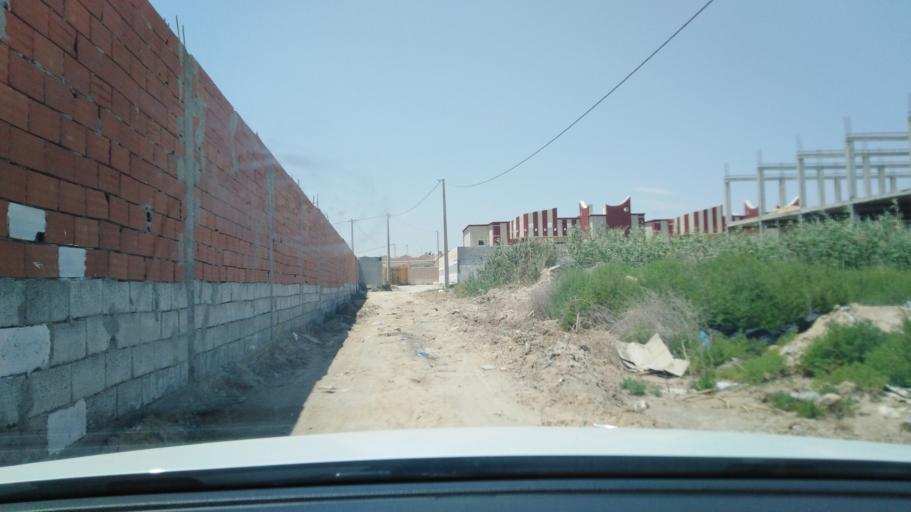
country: TN
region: Qabis
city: Gabes
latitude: 33.9462
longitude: 10.0740
